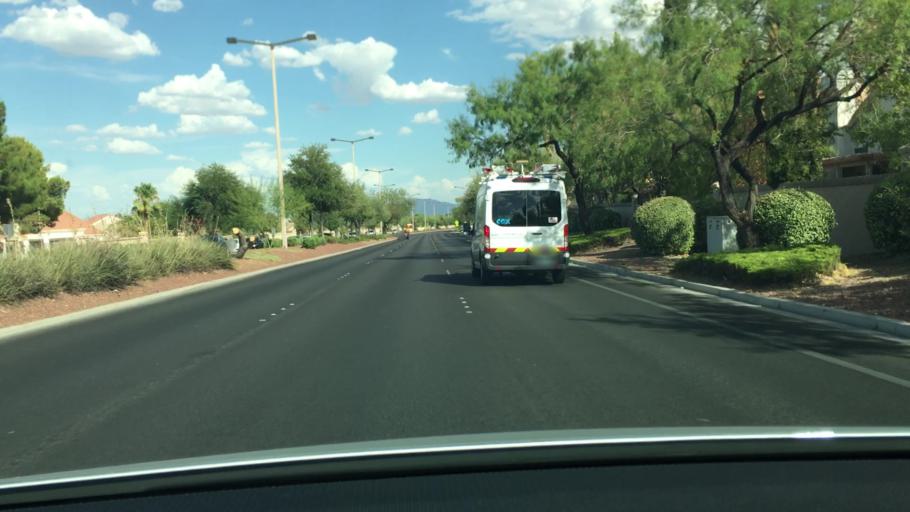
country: US
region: Nevada
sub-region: Clark County
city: Summerlin South
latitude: 36.2058
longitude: -115.2986
